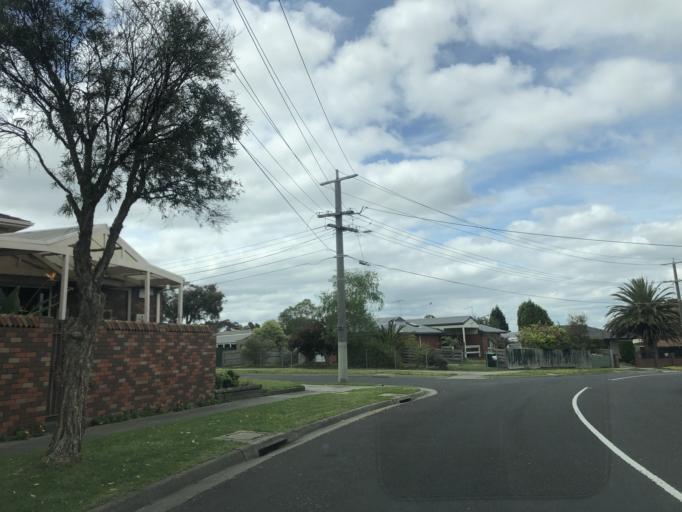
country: AU
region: Victoria
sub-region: Greater Dandenong
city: Dandenong North
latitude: -37.9531
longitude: 145.2130
